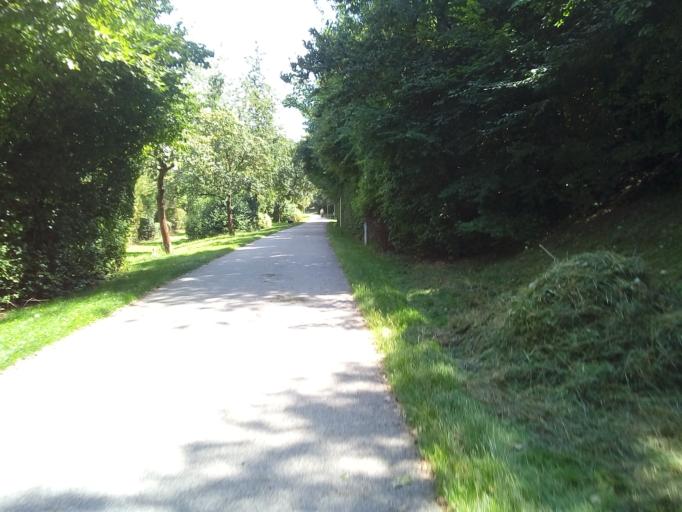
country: DE
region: Bavaria
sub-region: Upper Bavaria
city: Bogenhausen
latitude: 48.1647
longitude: 11.6352
